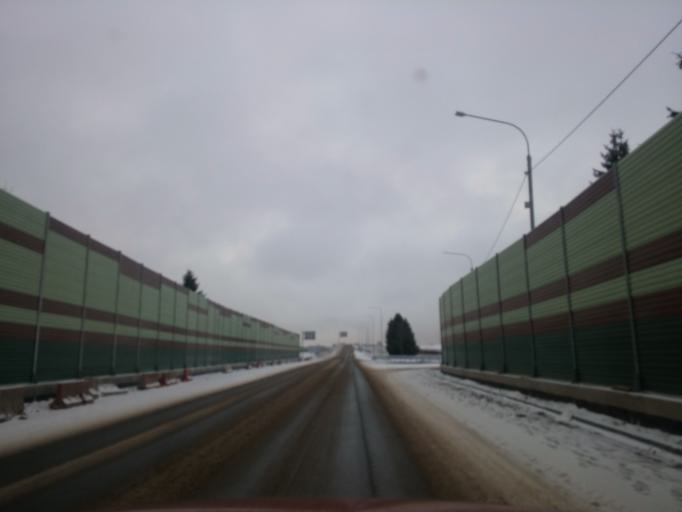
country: RU
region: Tverskaya
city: Likhoslavl'
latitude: 56.9839
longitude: 35.4396
